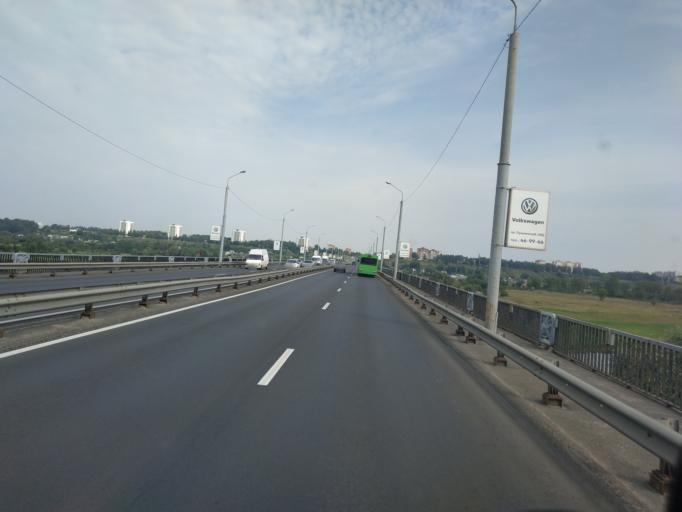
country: BY
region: Mogilev
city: Mahilyow
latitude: 53.8905
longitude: 30.3758
